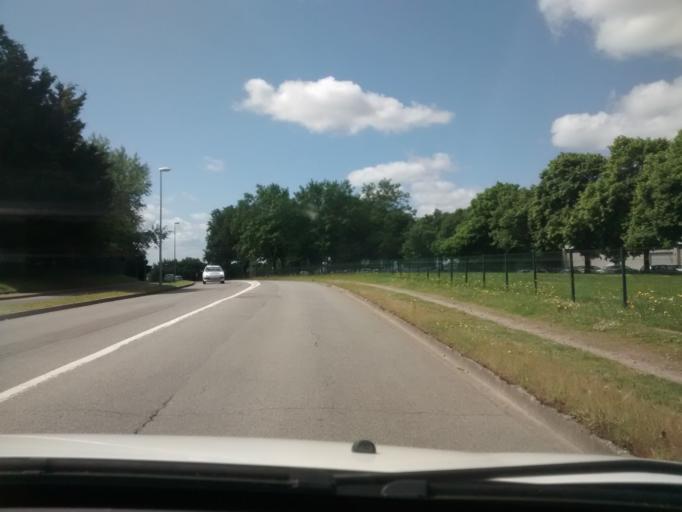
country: FR
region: Brittany
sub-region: Departement d'Ille-et-Vilaine
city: Cesson-Sevigne
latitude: 48.1241
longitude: -1.6284
